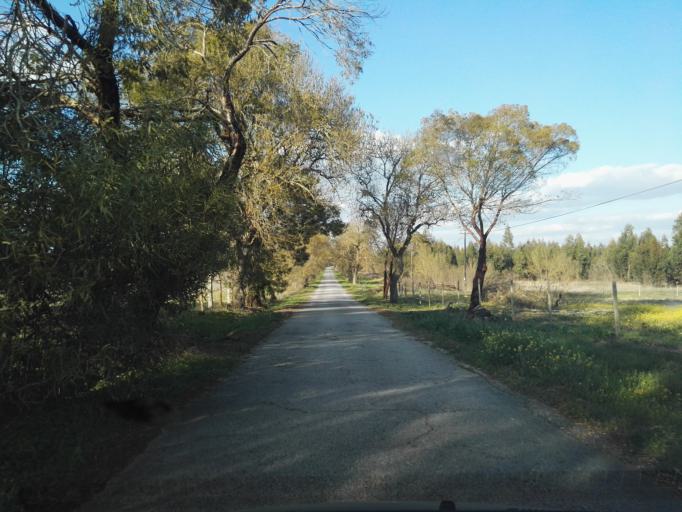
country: PT
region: Evora
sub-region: Evora
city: Evora
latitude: 38.5407
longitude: -7.9385
